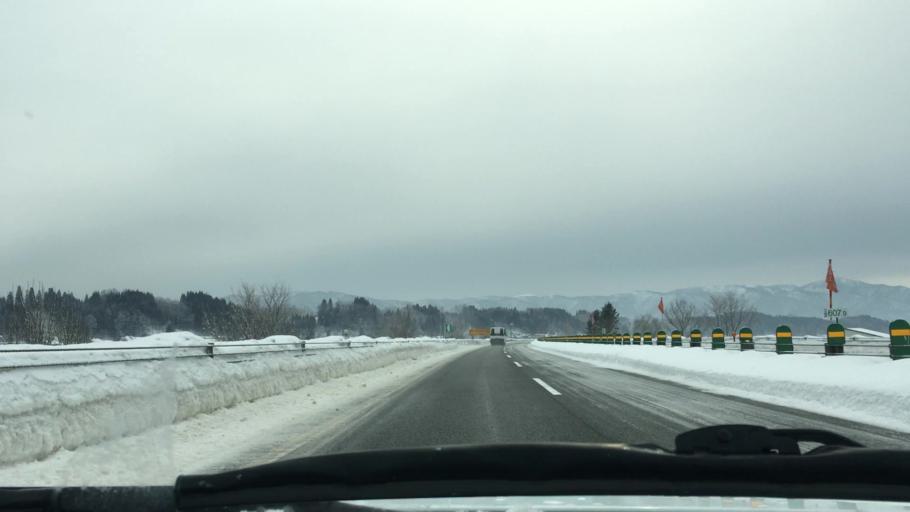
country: JP
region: Akita
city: Hanawa
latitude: 40.2992
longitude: 140.7493
